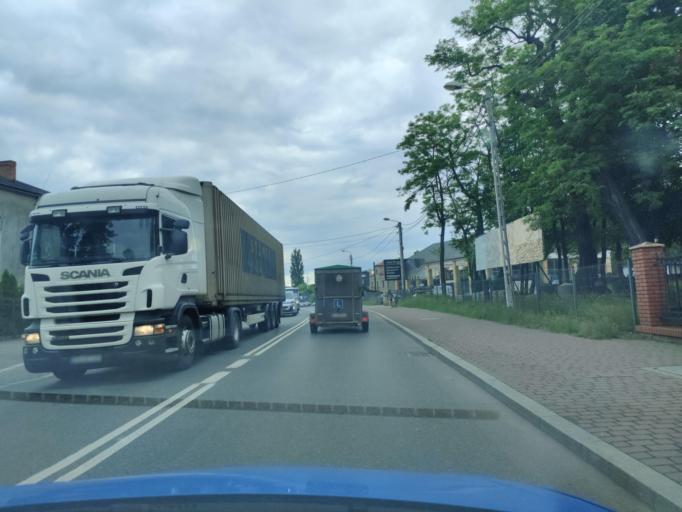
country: PL
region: Silesian Voivodeship
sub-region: Myslowice
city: Myslowice
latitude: 50.2378
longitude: 19.1571
